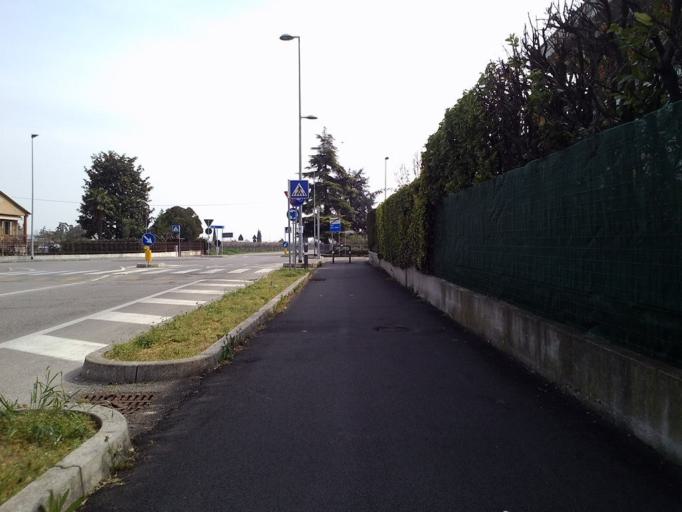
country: IT
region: Veneto
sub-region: Provincia di Verona
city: Dossobuono
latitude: 45.3876
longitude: 10.9175
